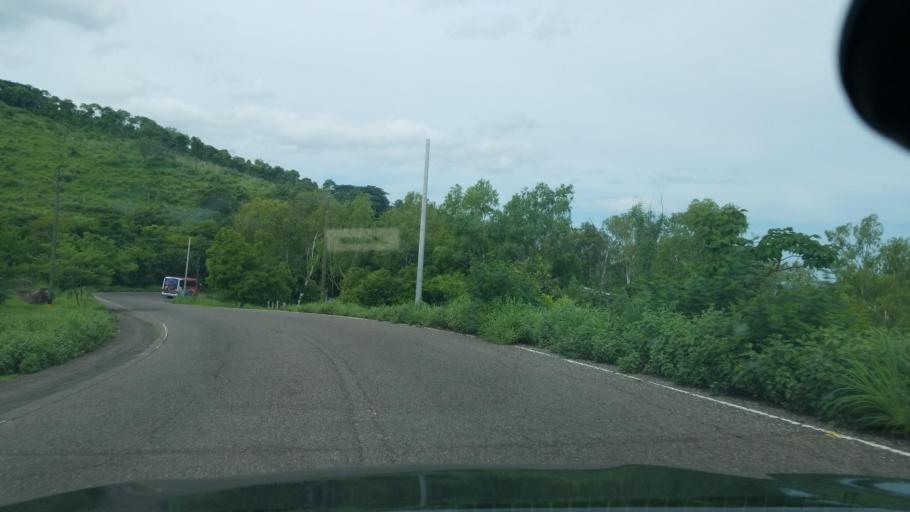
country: HN
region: Choluteca
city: Santa Ana de Yusguare
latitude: 13.3744
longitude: -87.0654
